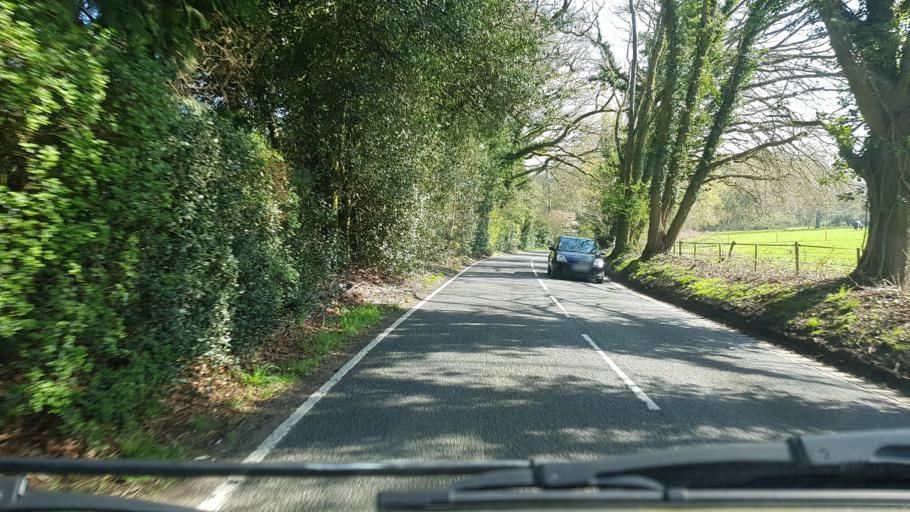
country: GB
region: England
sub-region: Surrey
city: Knaphill
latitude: 51.2923
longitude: -0.6100
